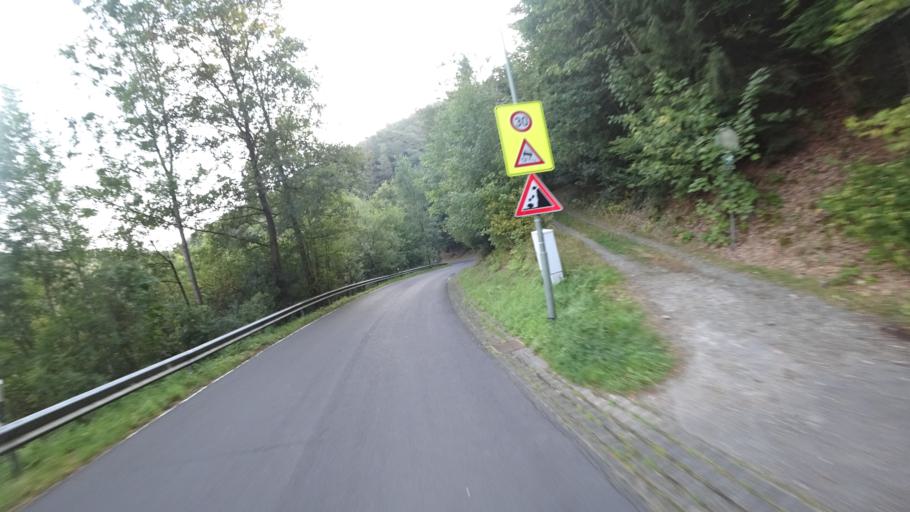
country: DE
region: Rheinland-Pfalz
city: Hohr-Grenzhausen
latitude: 50.4483
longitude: 7.6583
